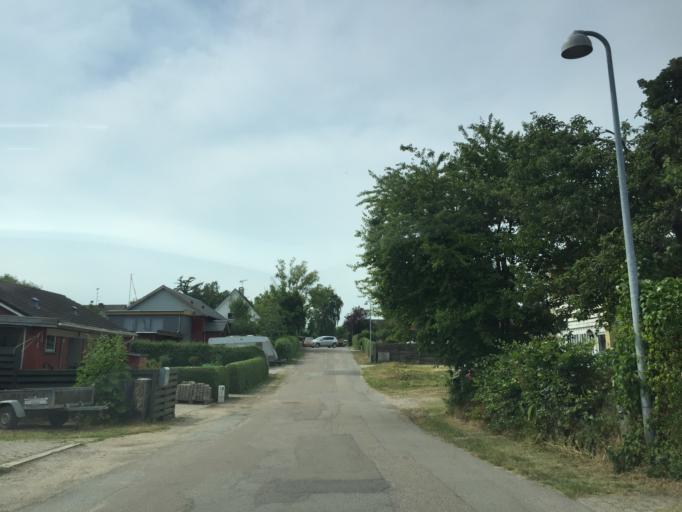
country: DK
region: Capital Region
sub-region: Hoje-Taastrup Kommune
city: Flong
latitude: 55.6530
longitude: 12.1910
